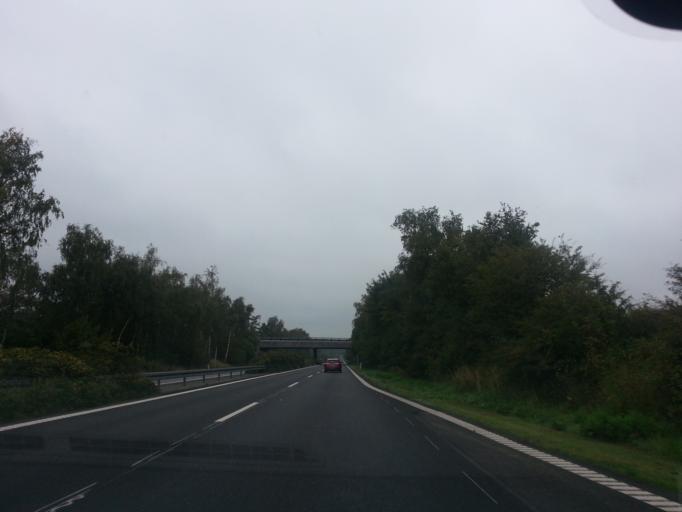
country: DK
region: Zealand
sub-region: Lolland Kommune
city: Maribo
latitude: 54.7603
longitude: 11.4622
